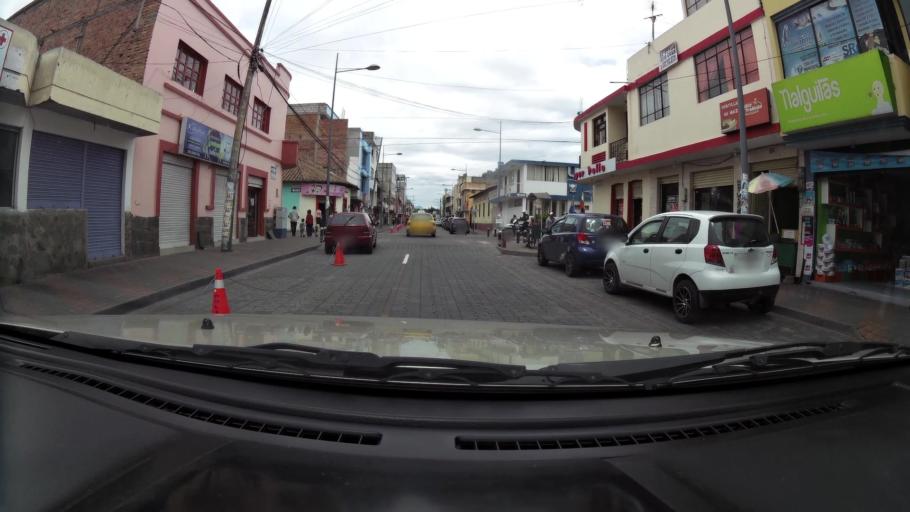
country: EC
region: Cotopaxi
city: San Miguel de Salcedo
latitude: -1.0338
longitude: -78.5889
